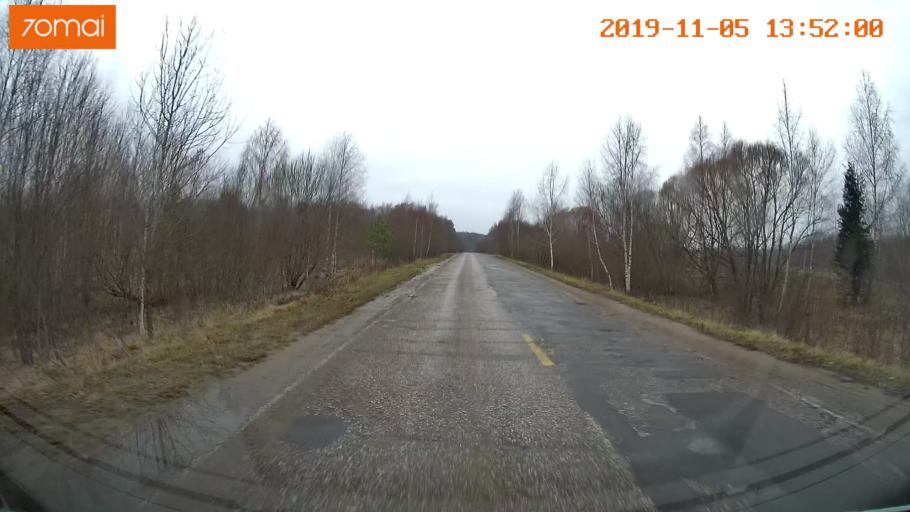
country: RU
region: Ivanovo
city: Kaminskiy
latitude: 57.0263
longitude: 41.3928
